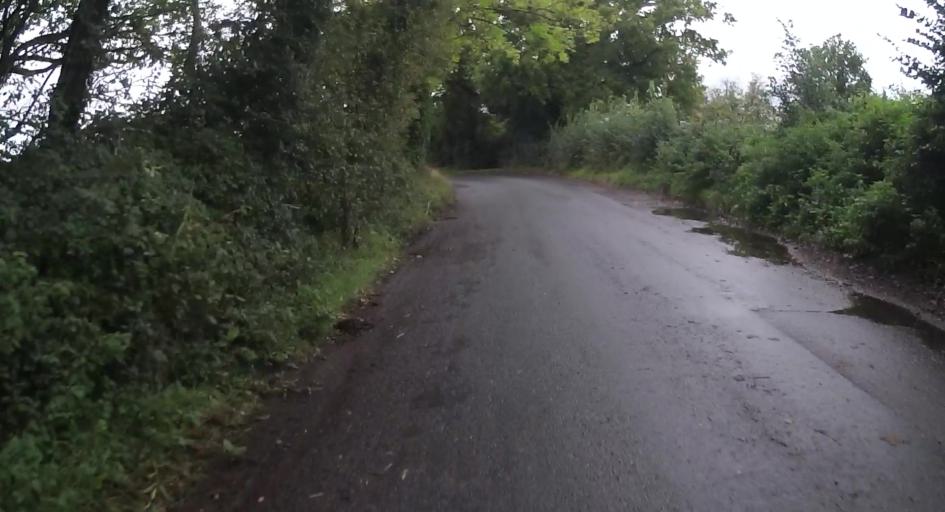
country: GB
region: England
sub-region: Hampshire
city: Tadley
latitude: 51.4125
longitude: -1.1766
